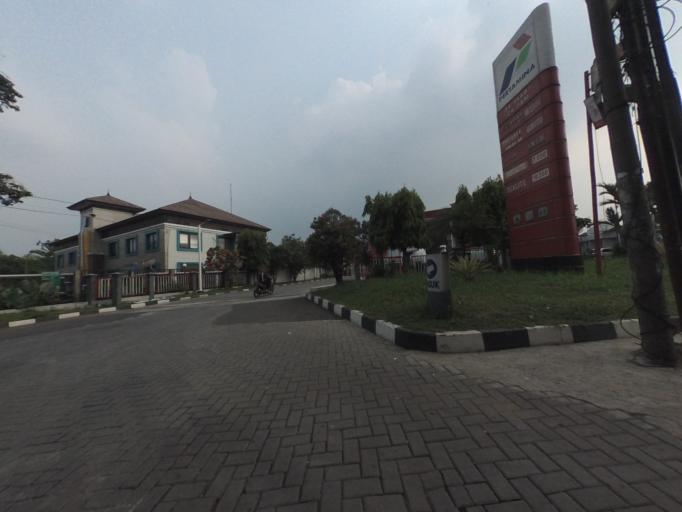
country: ID
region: West Java
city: Ciampea
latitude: -6.5641
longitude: 106.6778
